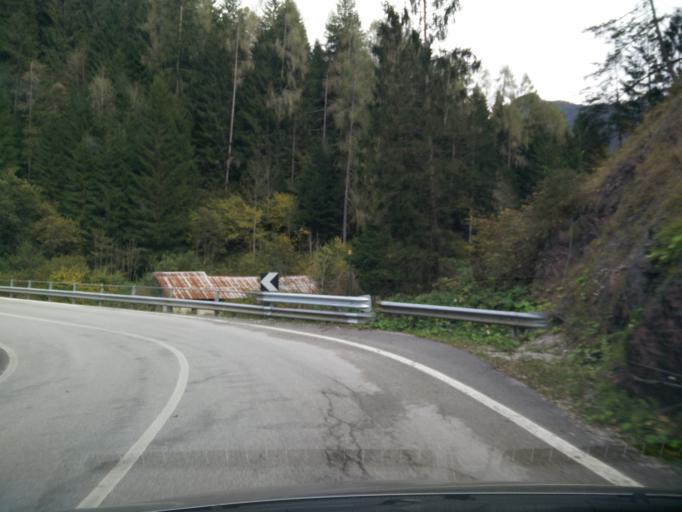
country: IT
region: Veneto
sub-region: Provincia di Belluno
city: Lorenzago di Cadore
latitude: 46.4872
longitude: 12.4675
